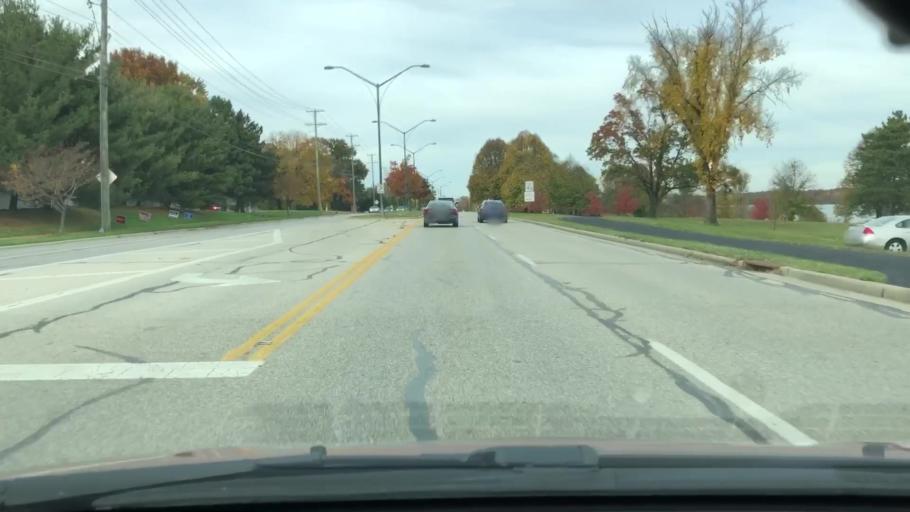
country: US
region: Ohio
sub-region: Franklin County
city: Huber Ridge
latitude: 40.1095
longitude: -82.8870
